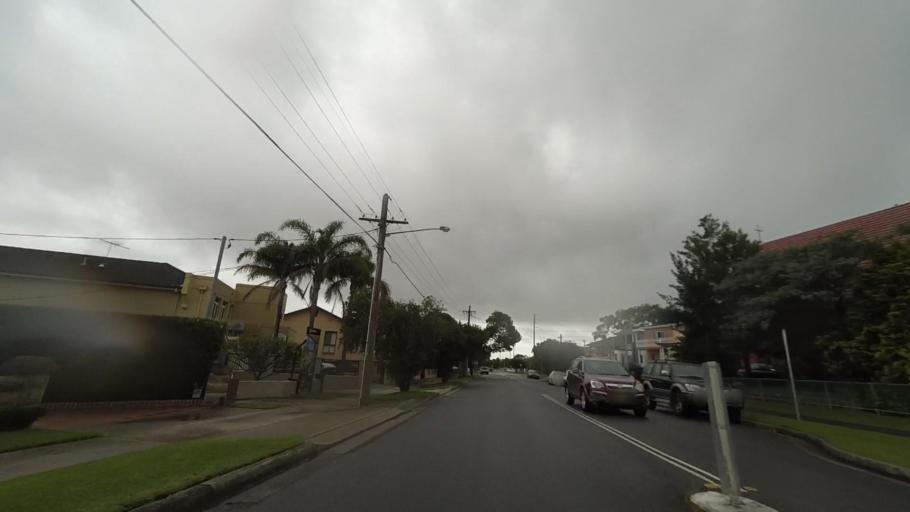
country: AU
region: New South Wales
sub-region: Kogarah
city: Kogarah Bay
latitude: -33.9924
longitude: 151.1285
